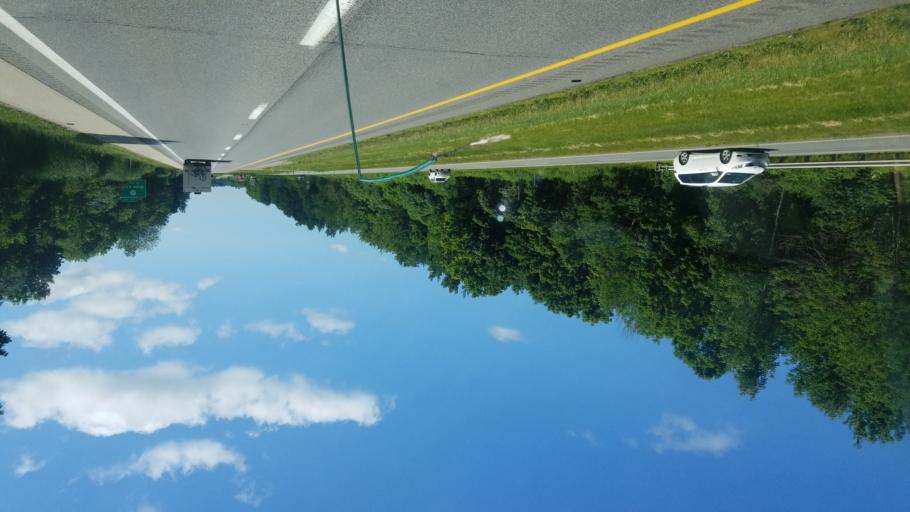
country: US
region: Pennsylvania
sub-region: Erie County
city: North East
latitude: 42.2087
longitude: -79.8047
